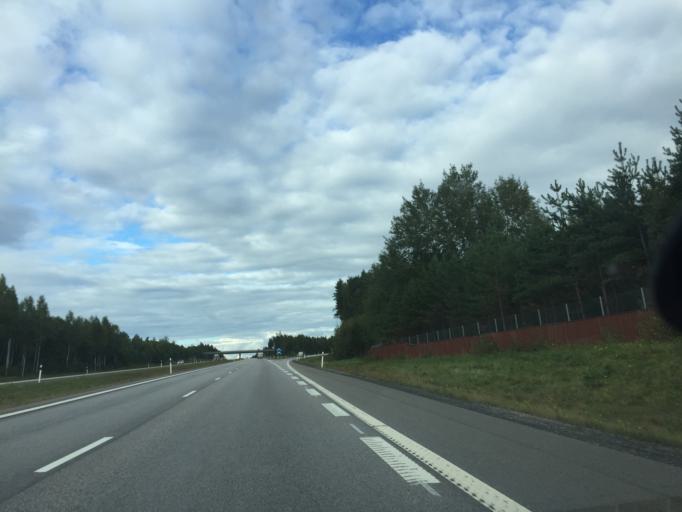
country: SE
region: OErebro
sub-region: Lindesbergs Kommun
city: Fellingsbro
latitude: 59.3367
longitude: 15.5359
